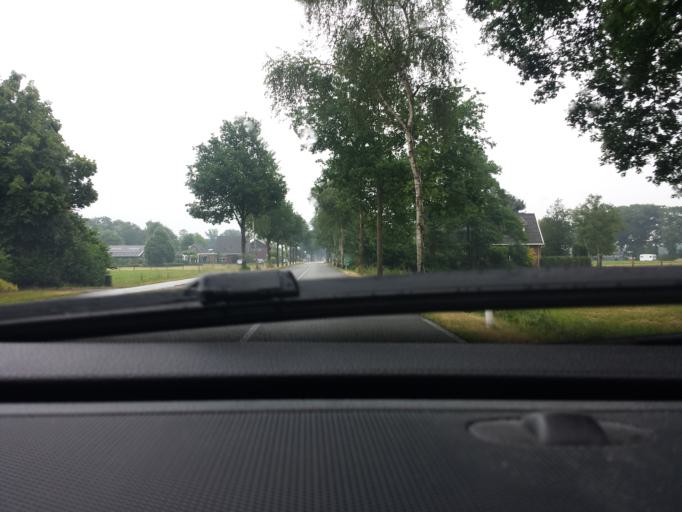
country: NL
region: Gelderland
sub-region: Berkelland
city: Eibergen
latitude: 52.1348
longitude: 6.6517
